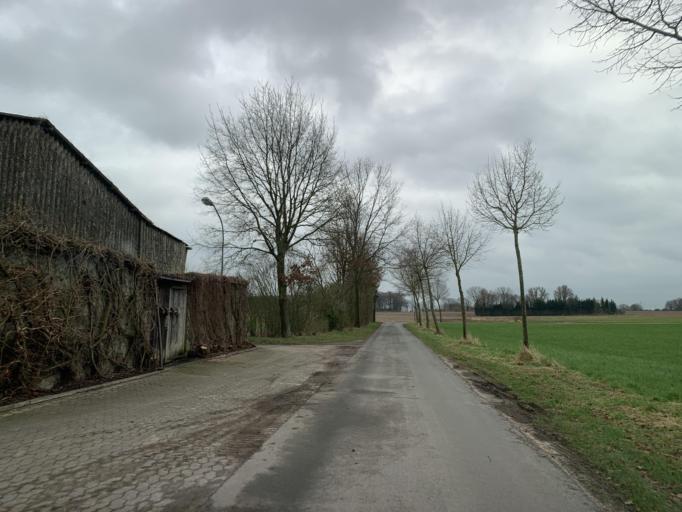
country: DE
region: North Rhine-Westphalia
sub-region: Regierungsbezirk Munster
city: Dulmen
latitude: 51.8491
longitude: 7.3254
